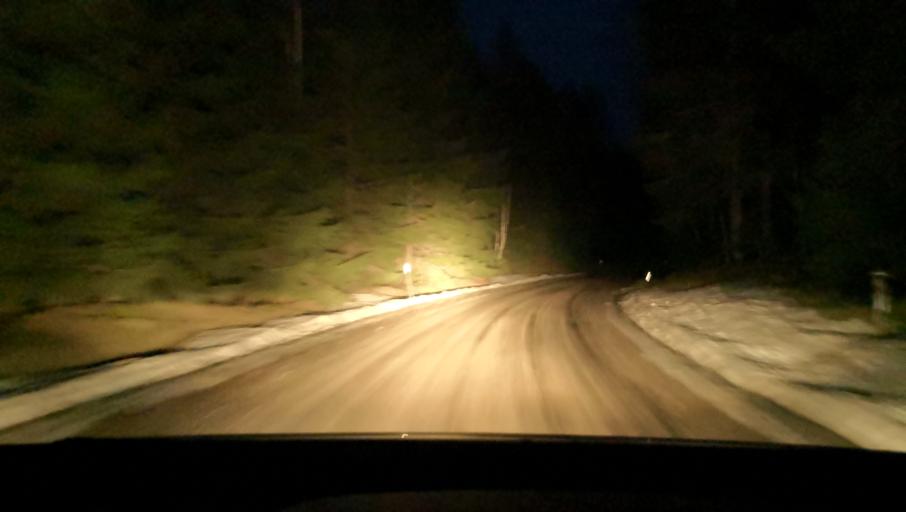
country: SE
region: Vaestmanland
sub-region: Skinnskattebergs Kommun
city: Skinnskatteberg
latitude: 59.6627
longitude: 15.5441
